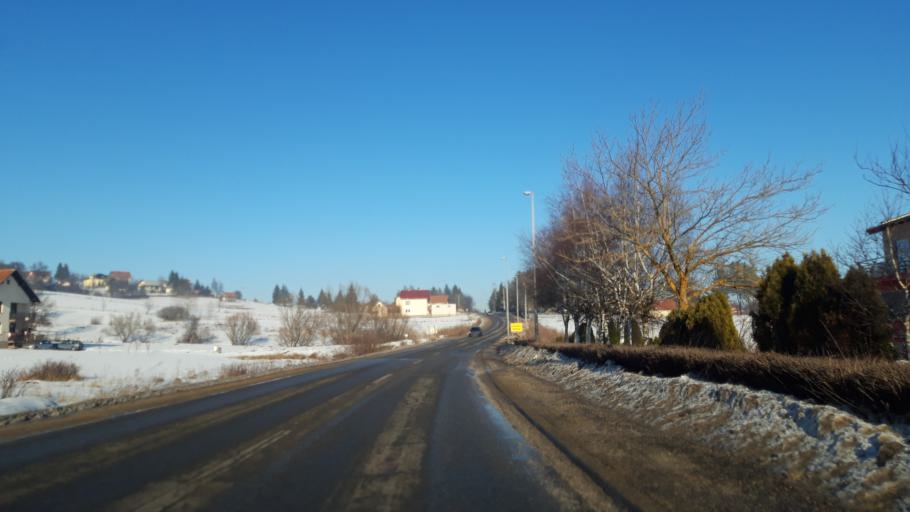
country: BA
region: Republika Srpska
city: Sokolac
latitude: 43.9254
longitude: 18.7826
